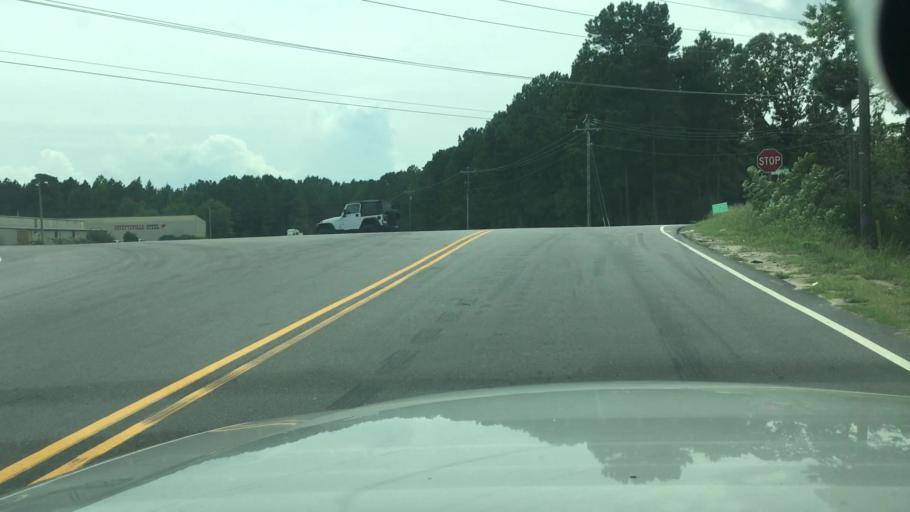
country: US
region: North Carolina
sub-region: Cumberland County
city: Hope Mills
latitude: 34.9597
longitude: -78.9009
